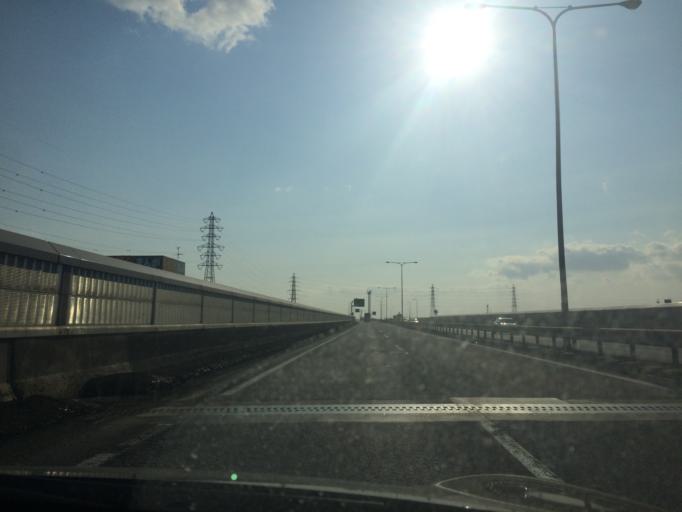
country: JP
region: Hokkaido
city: Sapporo
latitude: 43.0925
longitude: 141.4057
